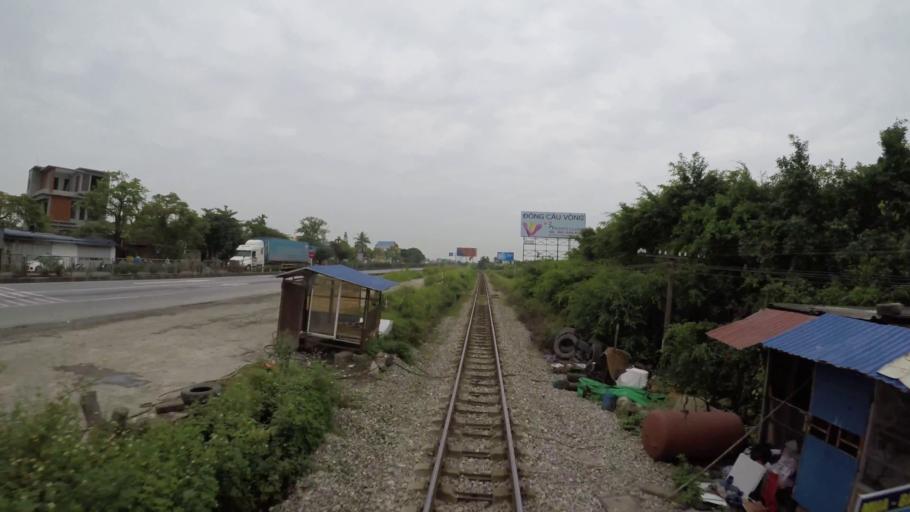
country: VN
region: Hai Duong
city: Phu Thai
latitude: 20.9359
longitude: 106.5497
